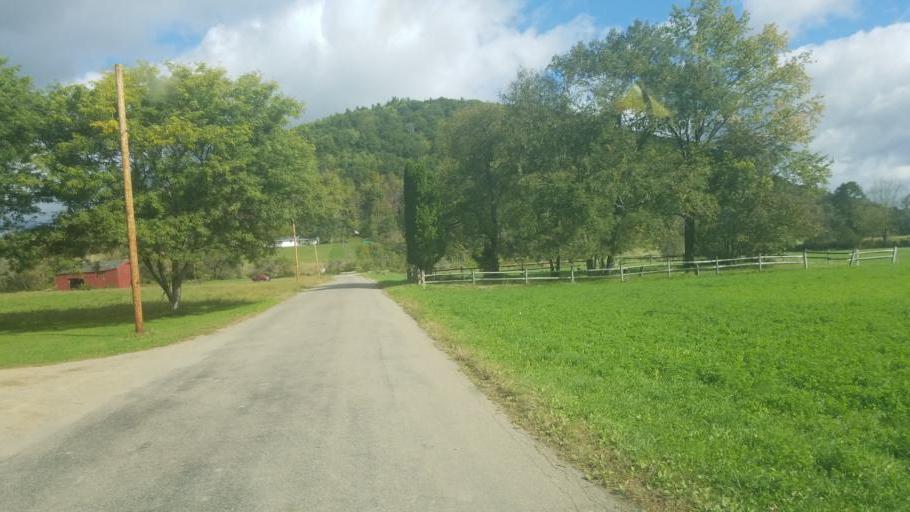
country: US
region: New York
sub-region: Cattaraugus County
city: Weston Mills
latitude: 42.1346
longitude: -78.3442
